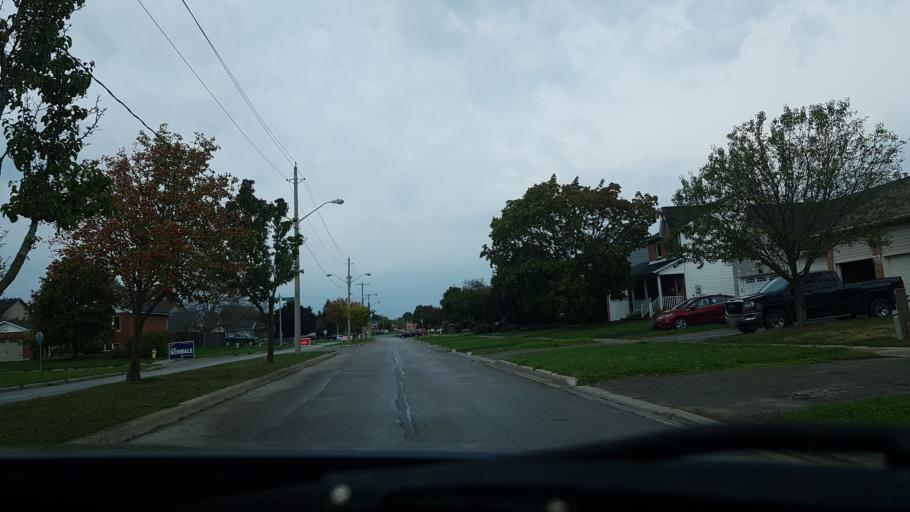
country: CA
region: Ontario
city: Omemee
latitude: 44.3679
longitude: -78.7472
